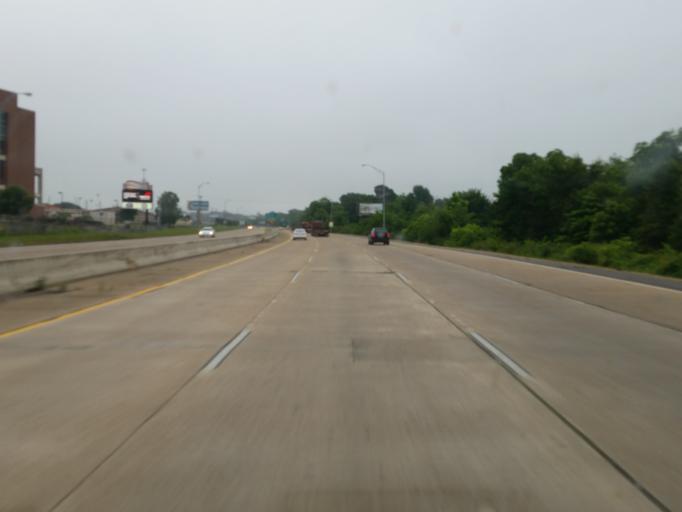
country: US
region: Louisiana
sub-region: Caddo Parish
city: Shreveport
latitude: 32.4731
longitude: -93.7939
